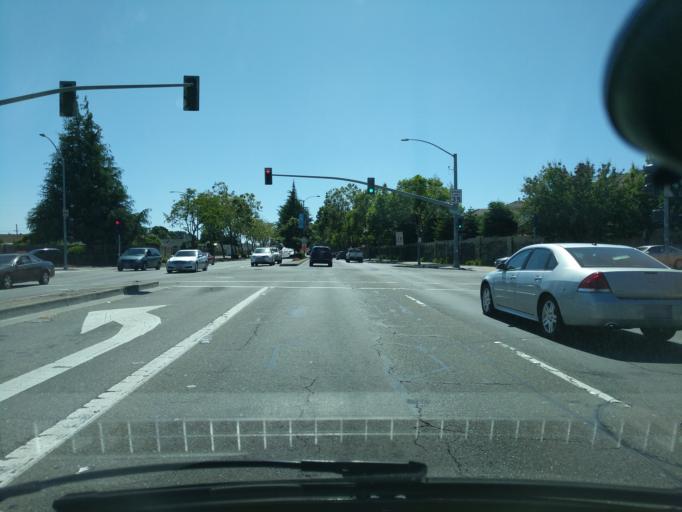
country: US
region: California
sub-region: Alameda County
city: San Leandro
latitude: 37.7212
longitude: -122.1704
